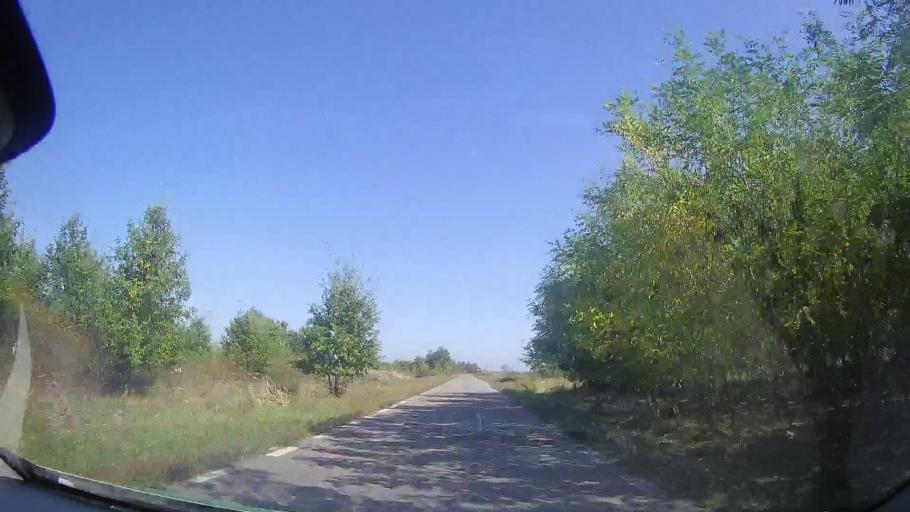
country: RO
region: Timis
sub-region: Comuna Ohaba Lunga
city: Ohaba Lunga
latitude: 45.9192
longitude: 21.9579
